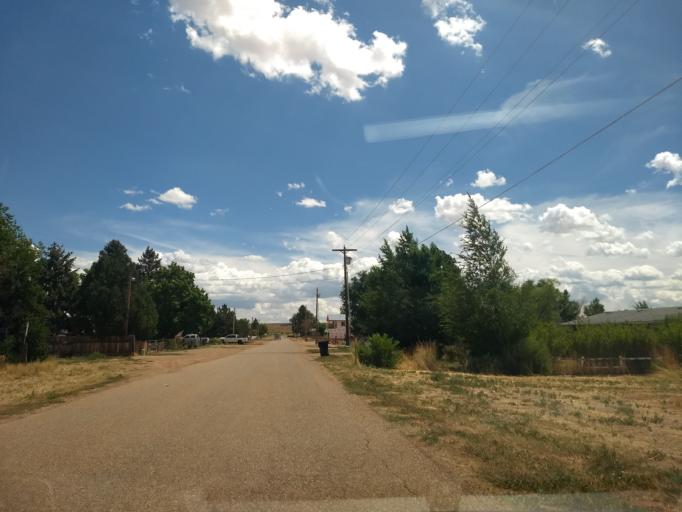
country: US
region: Arizona
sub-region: Coconino County
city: Fredonia
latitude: 36.9473
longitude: -112.5223
